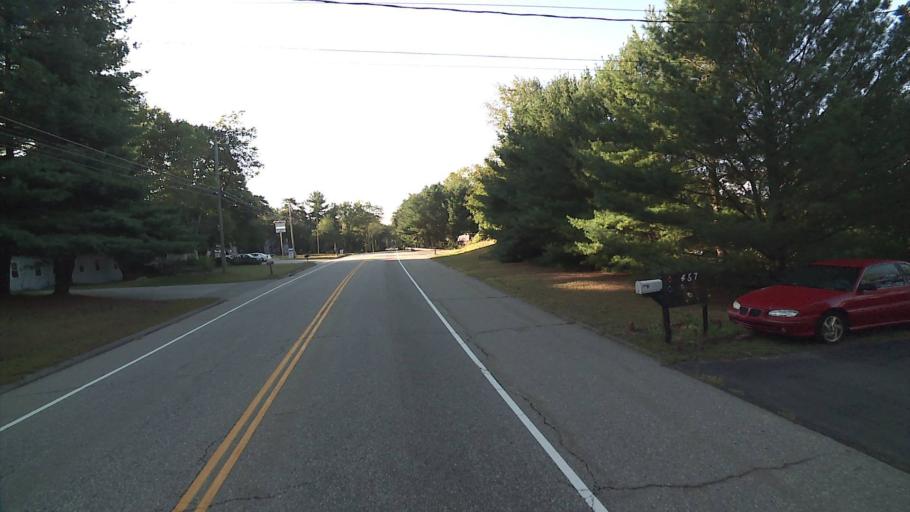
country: US
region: Connecticut
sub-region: Tolland County
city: Mansfield City
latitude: 41.7569
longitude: -72.2641
